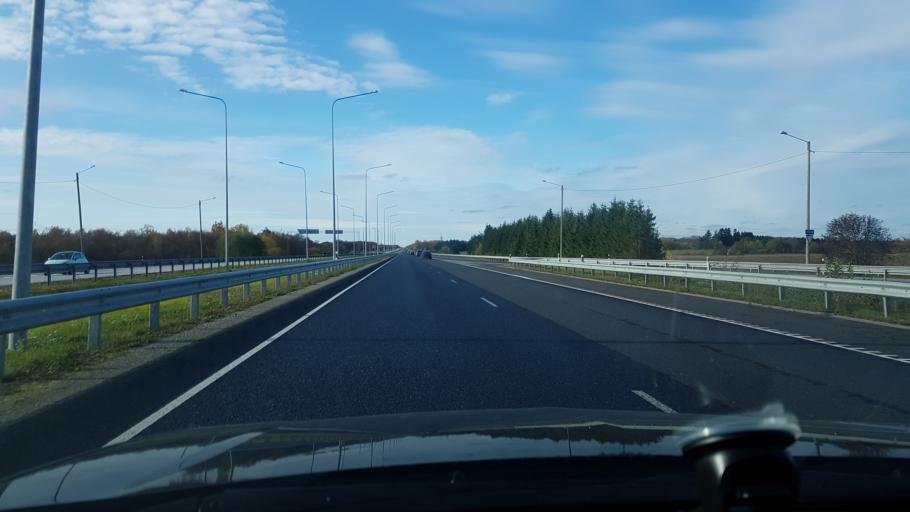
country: EE
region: Harju
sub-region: Kuusalu vald
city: Kuusalu
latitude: 59.4451
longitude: 25.3723
